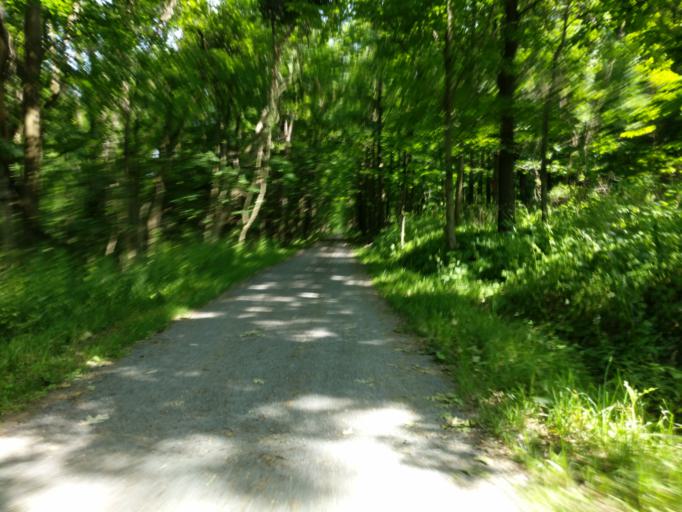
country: US
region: New York
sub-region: Tompkins County
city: Northwest Ithaca
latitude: 42.5044
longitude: -76.5496
